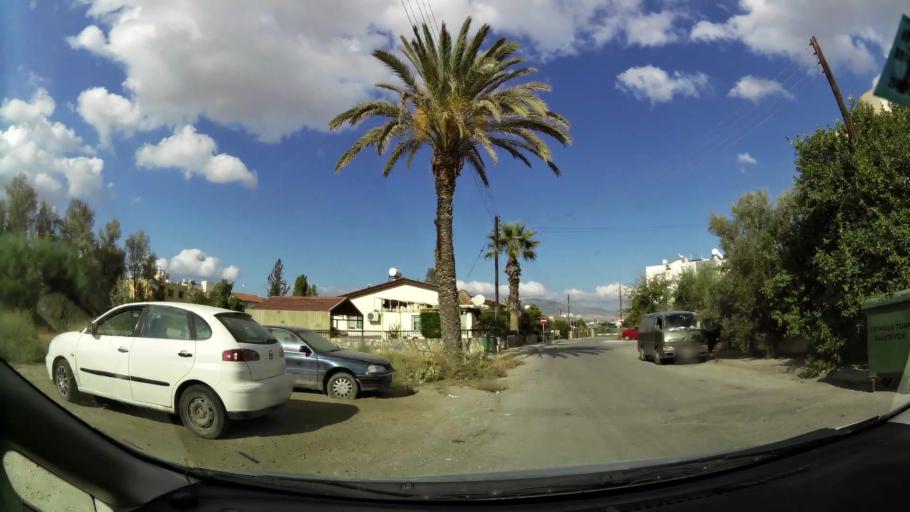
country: CY
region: Lefkosia
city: Nicosia
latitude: 35.2006
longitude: 33.3517
